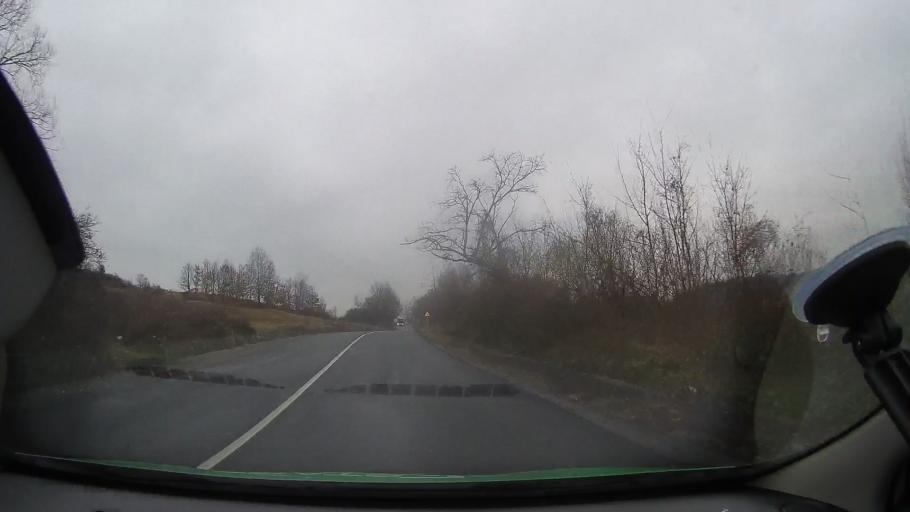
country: RO
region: Arad
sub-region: Comuna Varfurile
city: Varfurile
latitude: 46.3269
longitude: 22.4924
